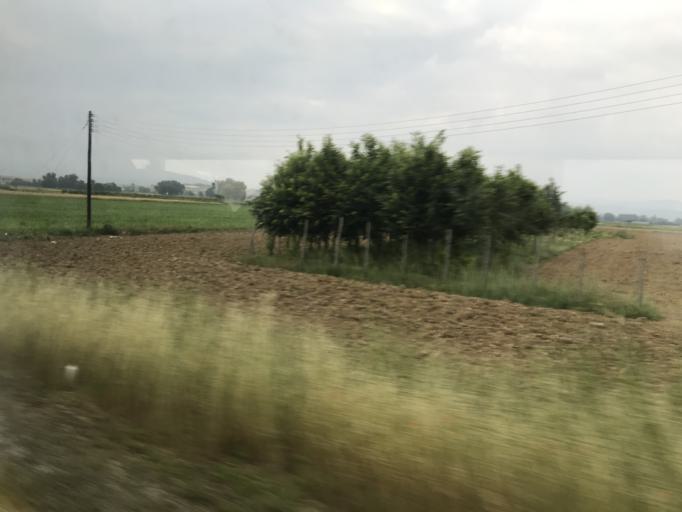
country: GR
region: East Macedonia and Thrace
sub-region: Nomos Rodopis
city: Arisvi
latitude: 41.0574
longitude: 25.6088
